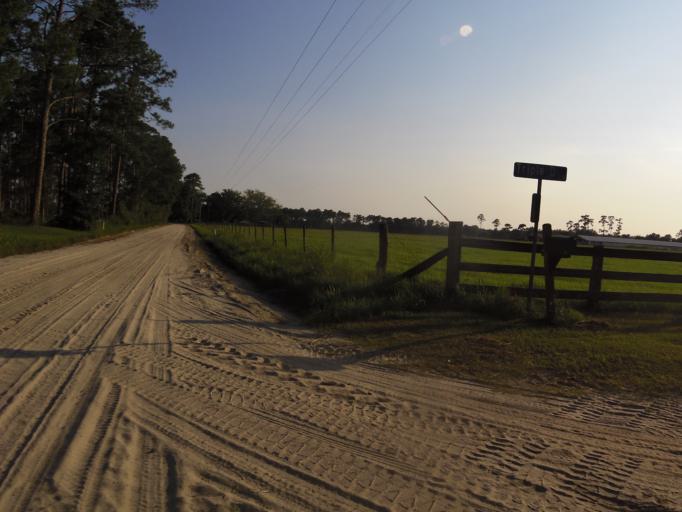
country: US
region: Florida
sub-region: Nassau County
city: Callahan
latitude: 30.5383
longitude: -81.9983
